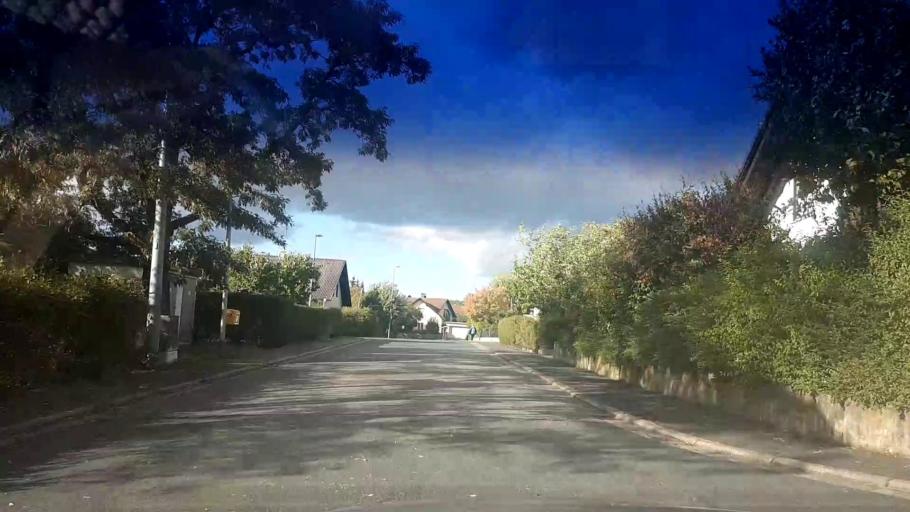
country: DE
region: Bavaria
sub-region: Upper Franconia
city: Gundelsheim
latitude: 49.9405
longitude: 10.9204
